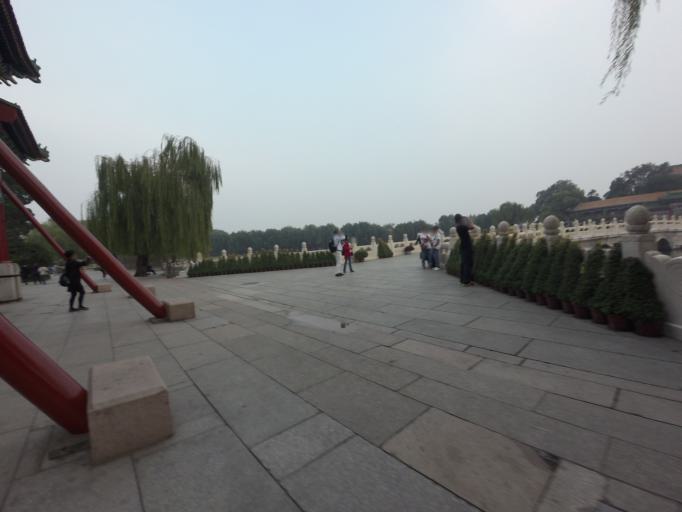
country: CN
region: Beijing
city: Beijing
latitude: 39.9228
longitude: 116.3830
